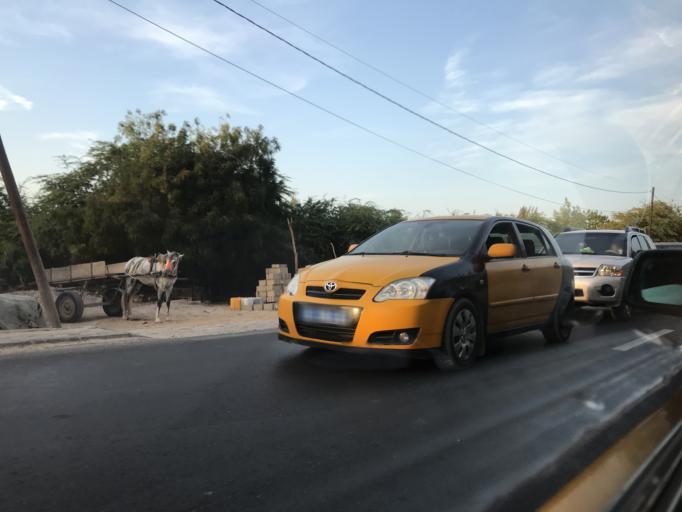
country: SN
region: Saint-Louis
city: Saint-Louis
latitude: 16.0380
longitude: -16.4606
